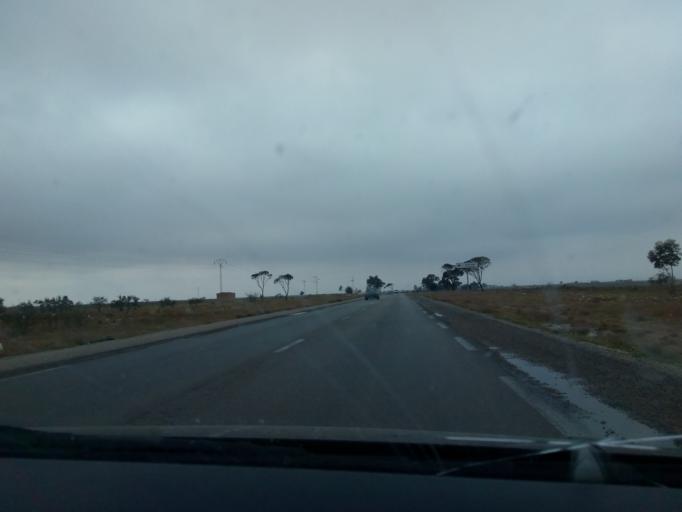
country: TN
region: Madanin
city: Medenine
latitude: 33.2747
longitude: 10.4685
